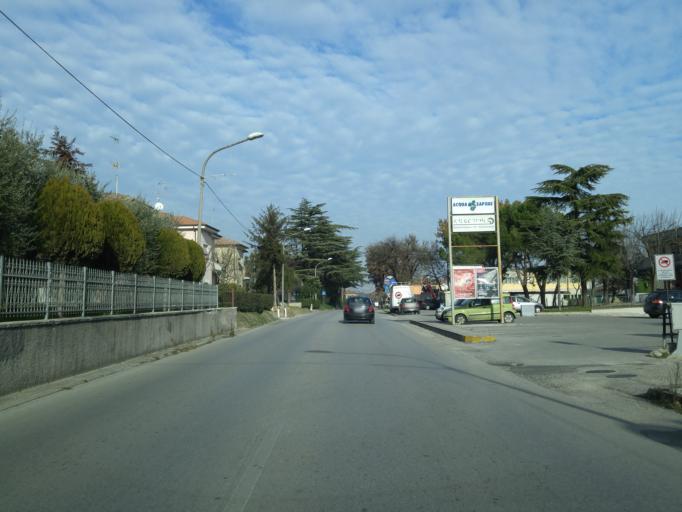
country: IT
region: The Marches
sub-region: Provincia di Pesaro e Urbino
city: Calcinelli
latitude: 43.7565
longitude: 12.9233
